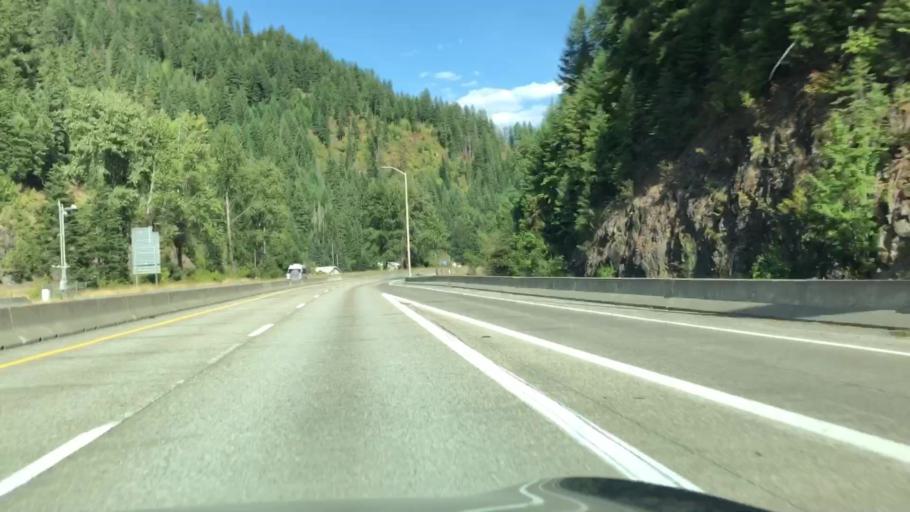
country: US
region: Idaho
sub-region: Shoshone County
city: Wallace
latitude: 47.4738
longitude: -115.9093
